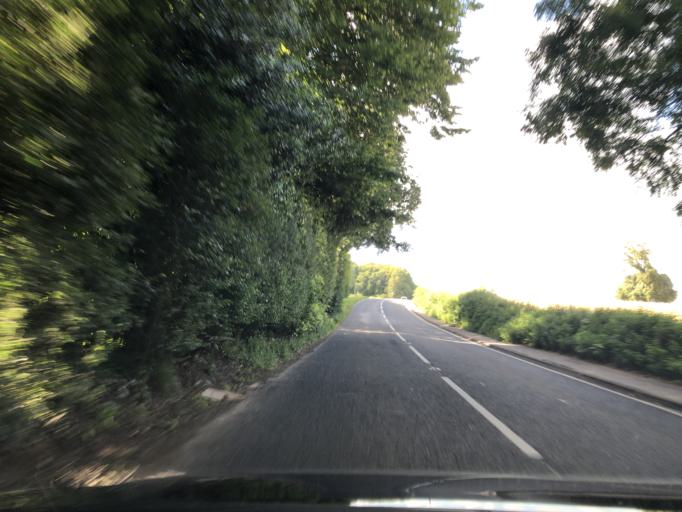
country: GB
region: Northern Ireland
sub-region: Ards District
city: Comber
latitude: 54.5608
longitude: -5.7623
